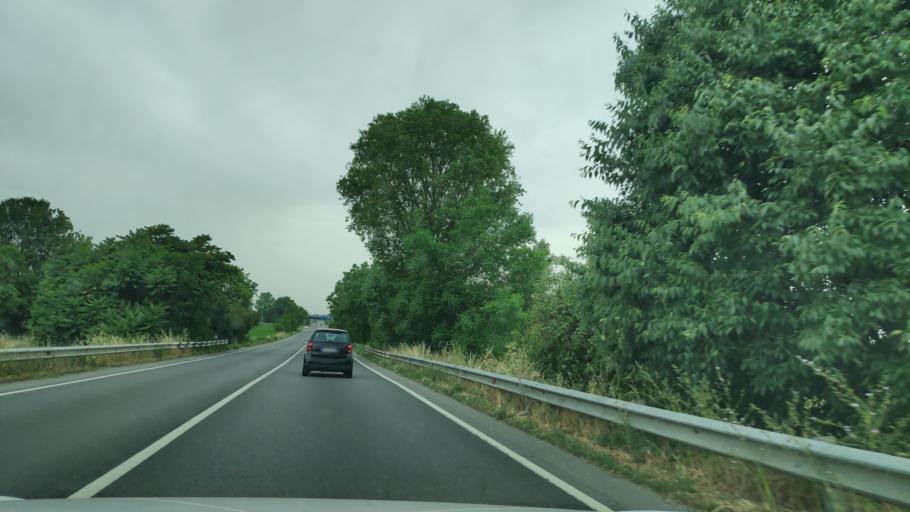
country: IT
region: Lombardy
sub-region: Provincia di Cremona
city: Soncino
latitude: 45.4042
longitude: 9.8568
